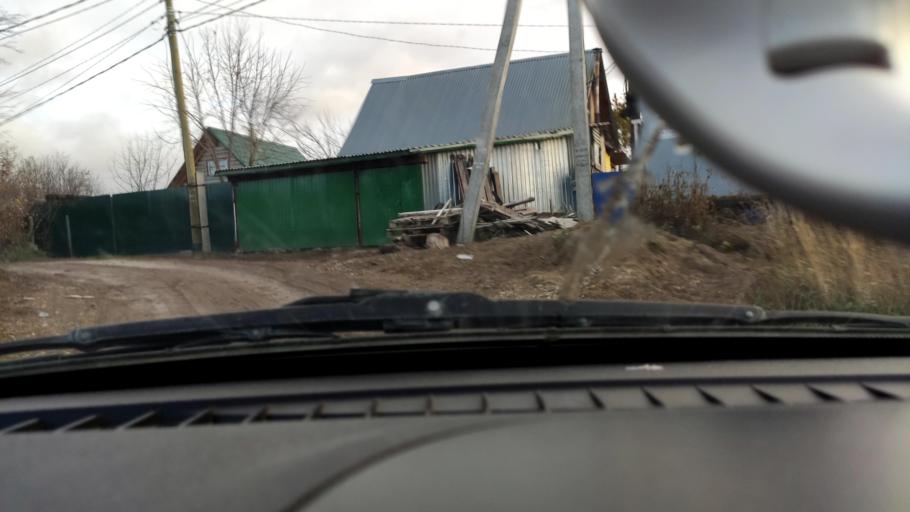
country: RU
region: Perm
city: Kondratovo
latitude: 57.9566
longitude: 56.1426
